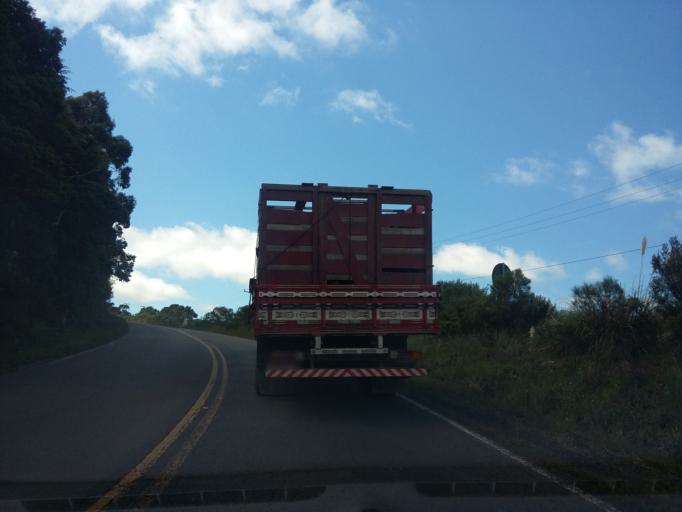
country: BR
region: Santa Catarina
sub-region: Sao Joaquim
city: Sao Joaquim
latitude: -28.2373
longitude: -49.8202
